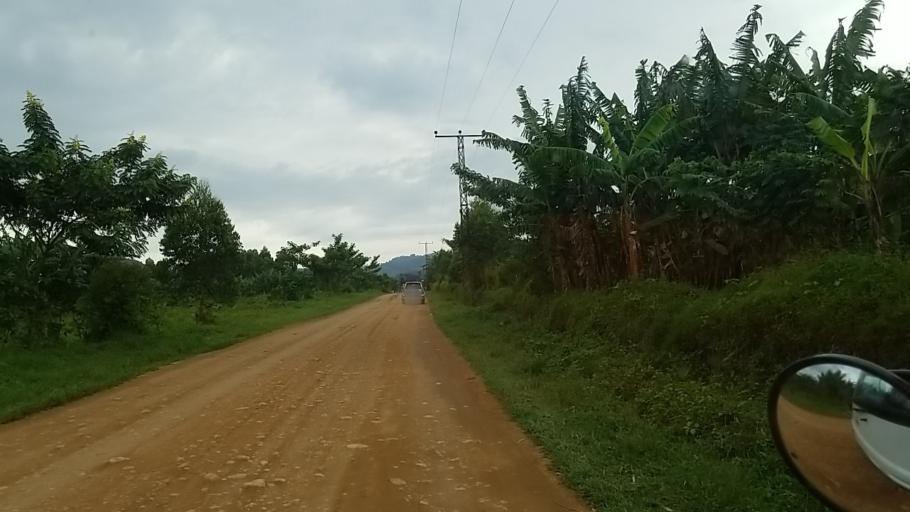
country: CD
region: Nord Kivu
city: Sake
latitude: -1.6807
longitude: 29.0163
